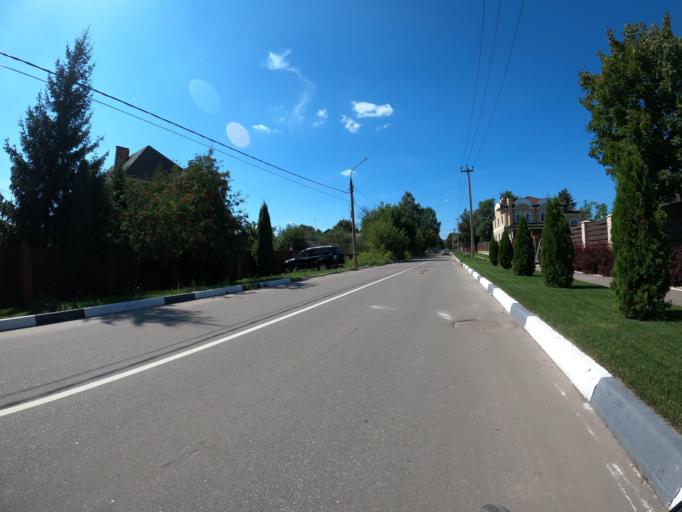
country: RU
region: Moskovskaya
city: Stupino
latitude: 54.8938
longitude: 38.0872
